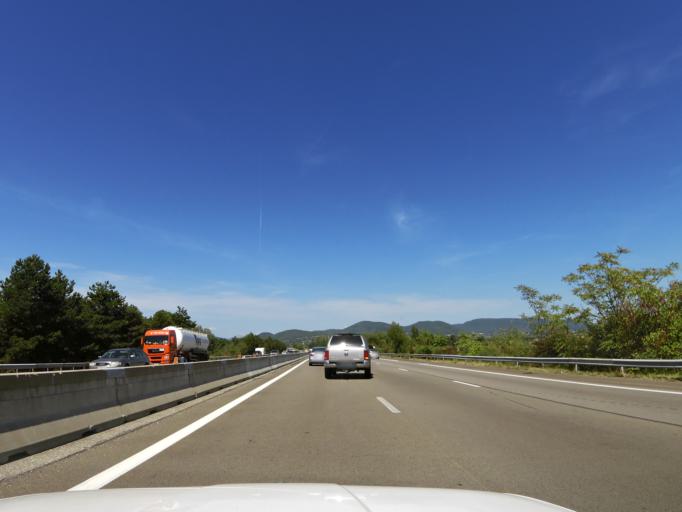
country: FR
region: Rhone-Alpes
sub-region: Departement de la Drome
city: Montboucher-sur-Jabron
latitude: 44.5603
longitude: 4.8113
